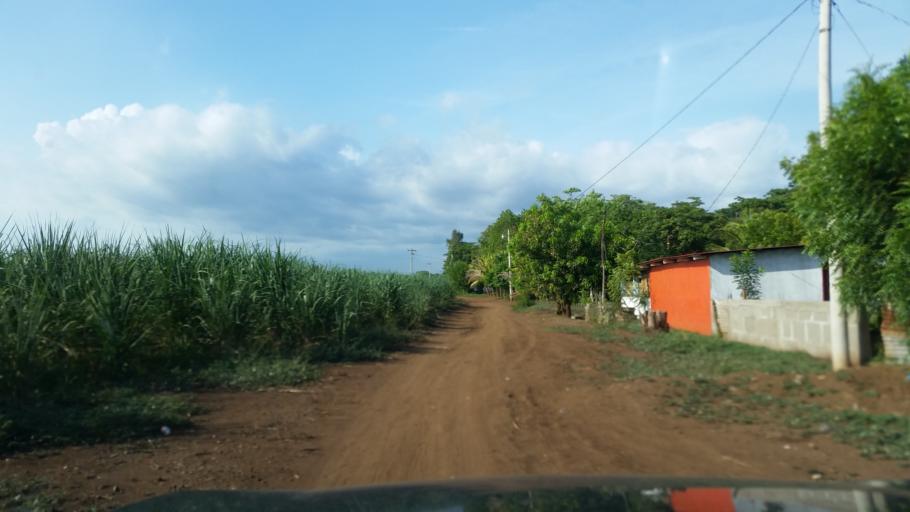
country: NI
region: Managua
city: Masachapa
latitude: 11.7908
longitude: -86.5107
